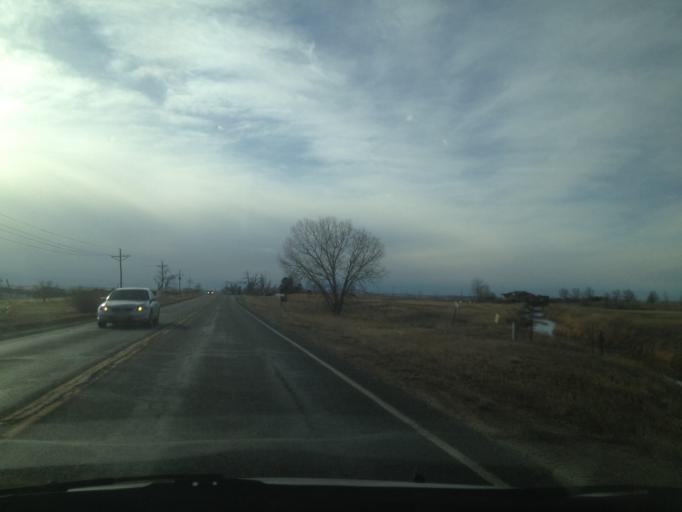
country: US
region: Colorado
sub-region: Weld County
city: Fort Lupton
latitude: 40.0803
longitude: -104.7866
